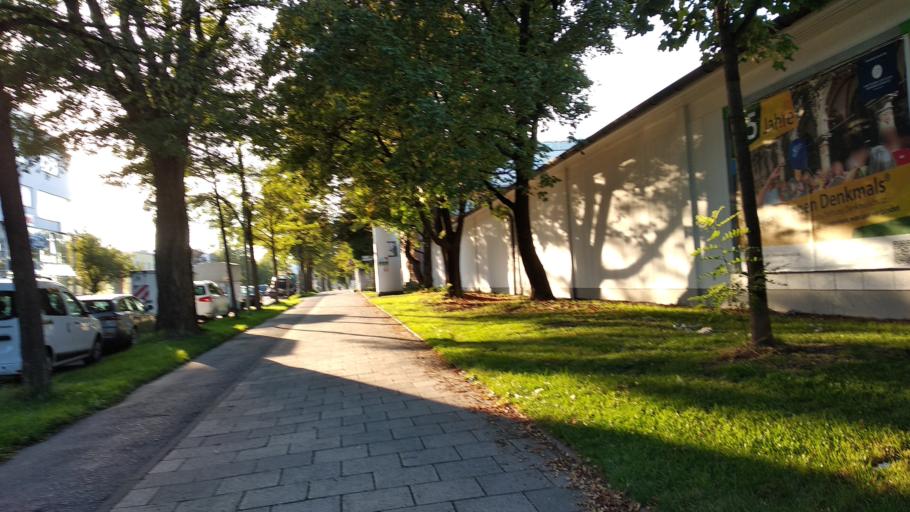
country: DE
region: Bavaria
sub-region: Upper Bavaria
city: Bogenhausen
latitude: 48.1311
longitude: 11.6294
